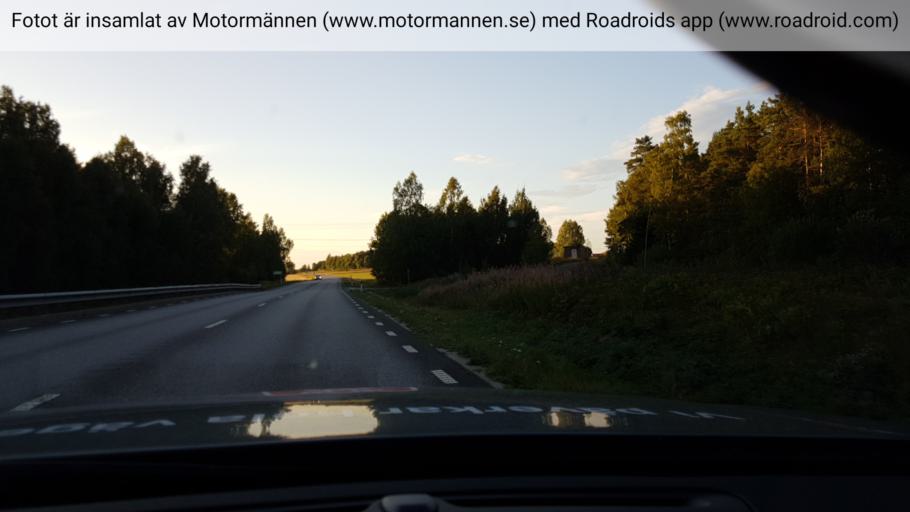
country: SE
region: OErebro
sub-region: Karlskoga Kommun
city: Karlskoga
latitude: 59.3651
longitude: 14.5079
